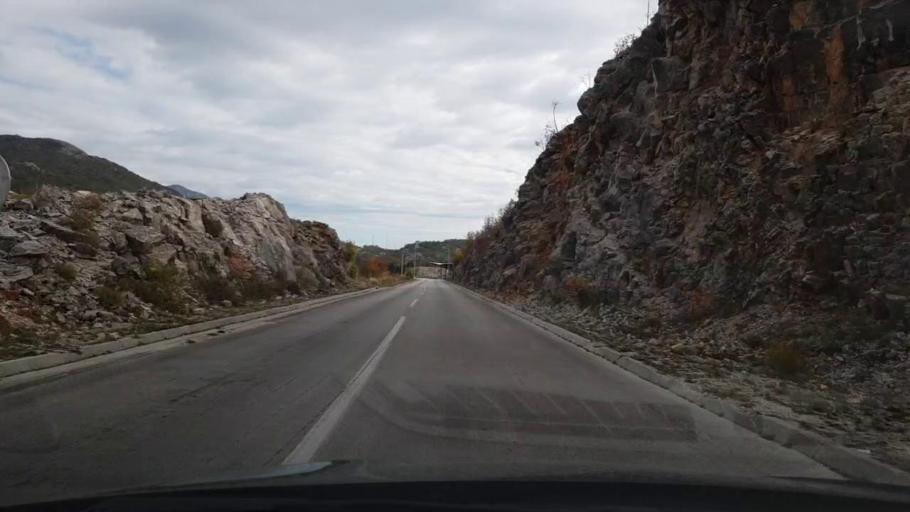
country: ME
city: Igalo
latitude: 42.5602
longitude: 18.4445
